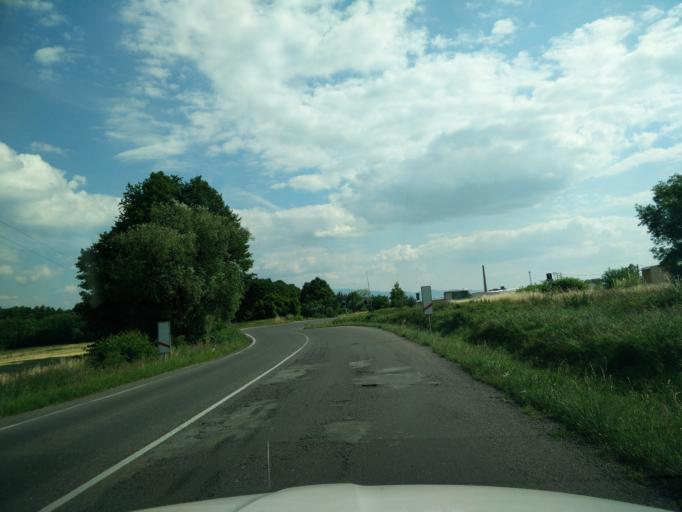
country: SK
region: Nitriansky
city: Prievidza
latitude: 48.8465
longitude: 18.6451
